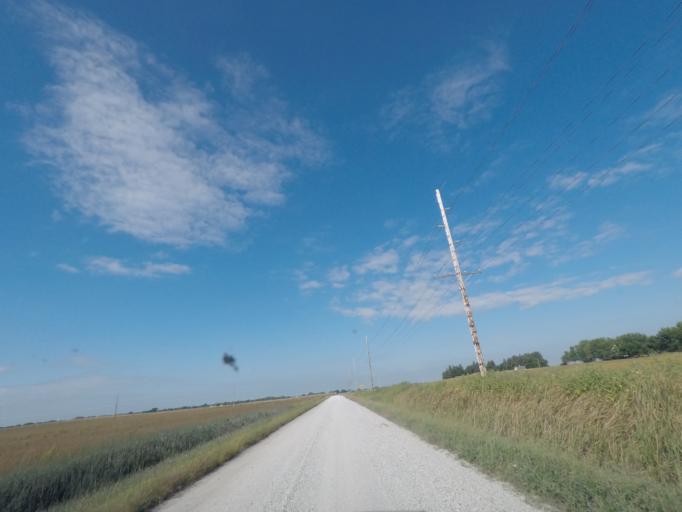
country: US
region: Iowa
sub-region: Story County
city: Nevada
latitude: 42.0345
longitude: -93.4219
